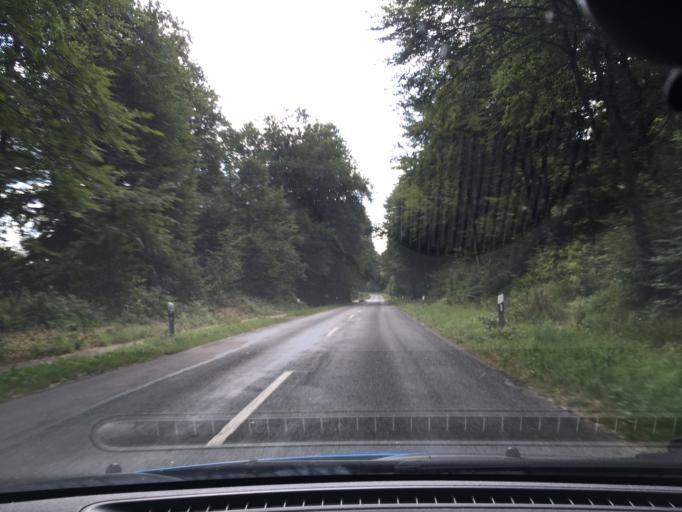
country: DE
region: Lower Saxony
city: Rehlingen
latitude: 53.0940
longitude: 10.2086
